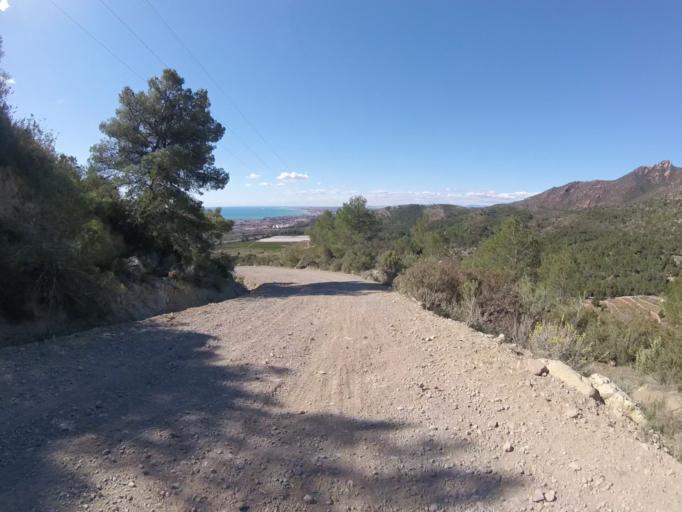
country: ES
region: Valencia
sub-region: Provincia de Castello
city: Benicassim
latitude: 40.0758
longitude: 0.0765
